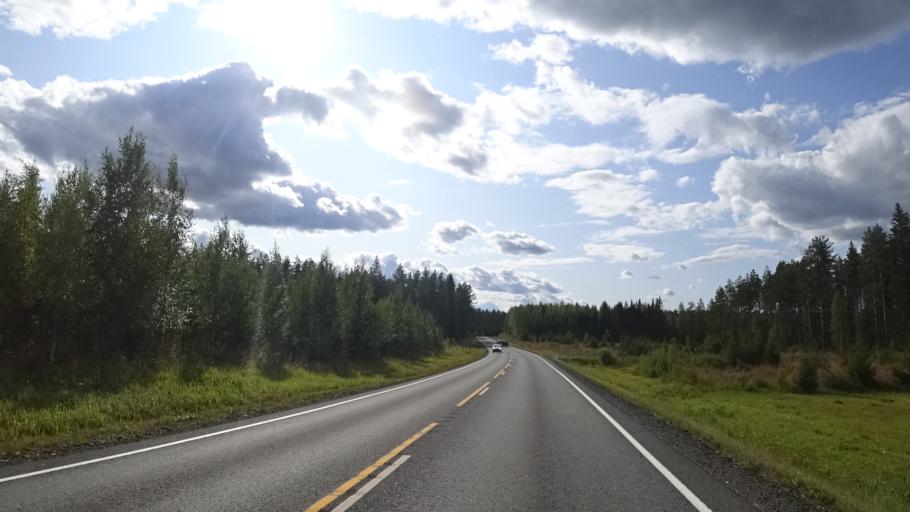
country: FI
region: North Karelia
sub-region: Keski-Karjala
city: Tohmajaervi
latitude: 62.1851
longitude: 30.4889
